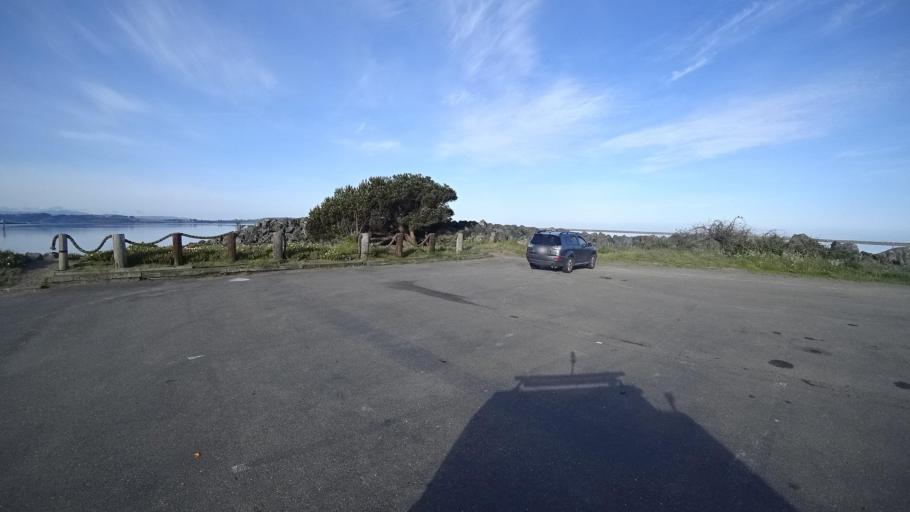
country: US
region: California
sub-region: Humboldt County
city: Humboldt Hill
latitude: 40.7368
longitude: -124.2202
